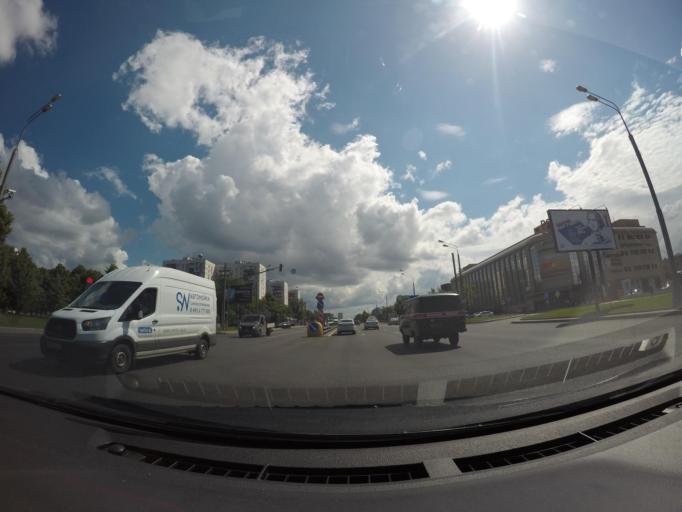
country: RU
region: Moscow
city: Novokuz'minki
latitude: 55.7189
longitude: 37.7830
